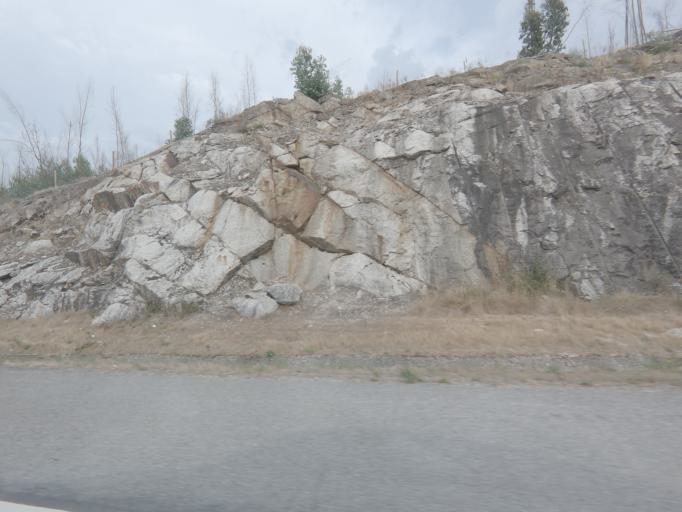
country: PT
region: Viseu
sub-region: Santa Comba Dao
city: Santa Comba Dao
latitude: 40.4484
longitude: -8.1060
